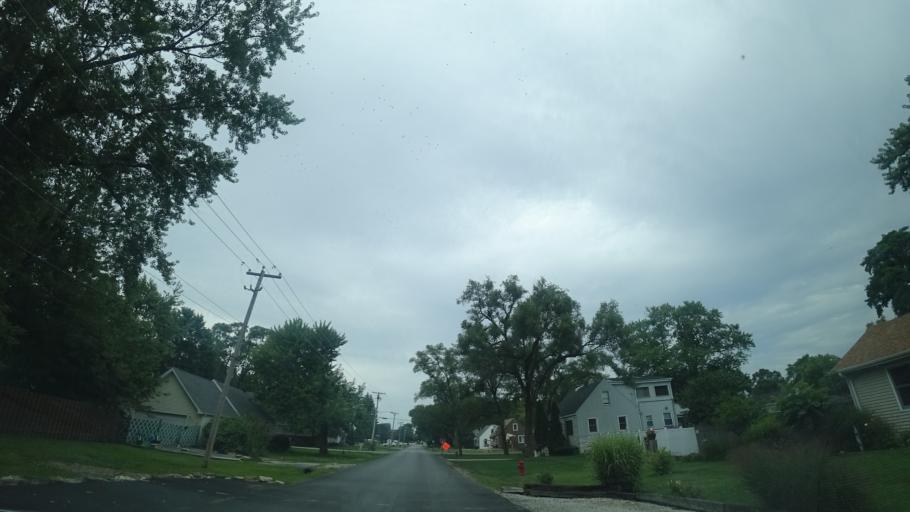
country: US
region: Illinois
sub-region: Cook County
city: Merrionette Park
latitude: 41.6792
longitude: -87.7149
